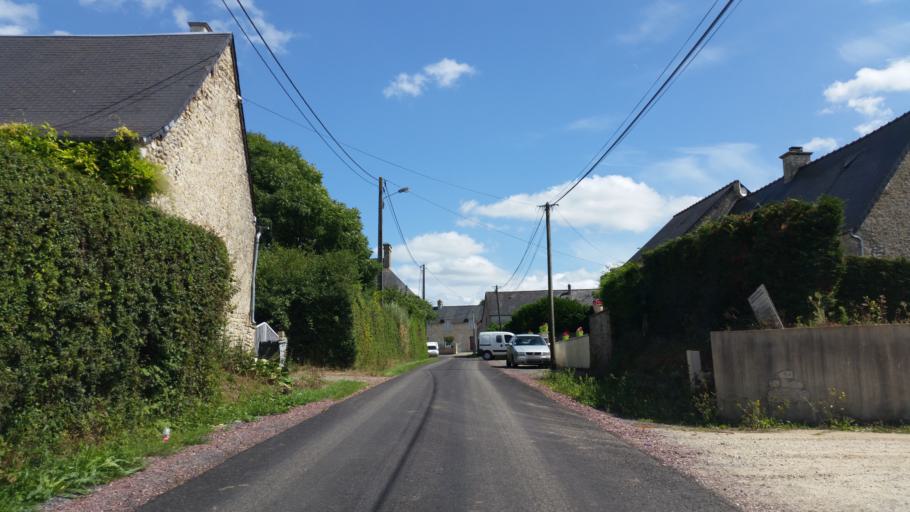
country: FR
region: Lower Normandy
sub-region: Departement de la Manche
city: Sainte-Mere-Eglise
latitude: 49.4584
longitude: -1.3199
